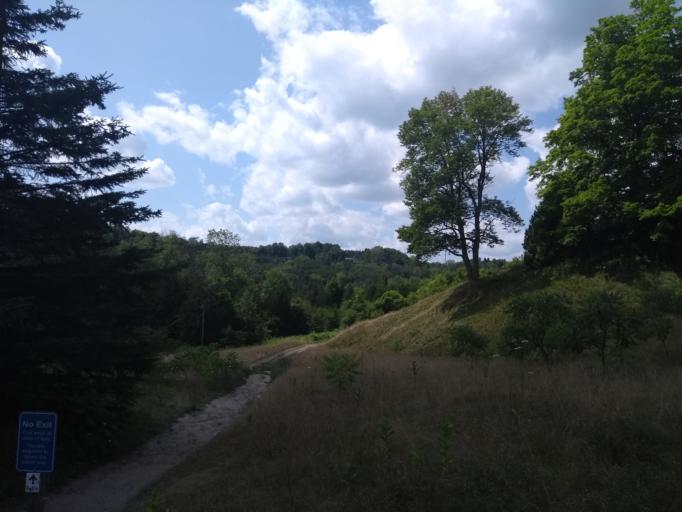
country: CA
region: Ontario
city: Orangeville
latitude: 43.8150
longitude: -80.0157
